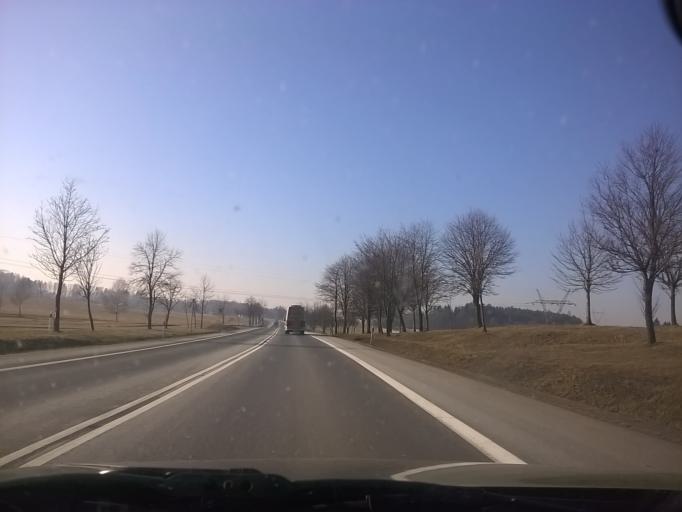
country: PL
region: Warmian-Masurian Voivodeship
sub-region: Powiat olsztynski
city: Olsztyn
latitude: 53.7867
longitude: 20.5892
